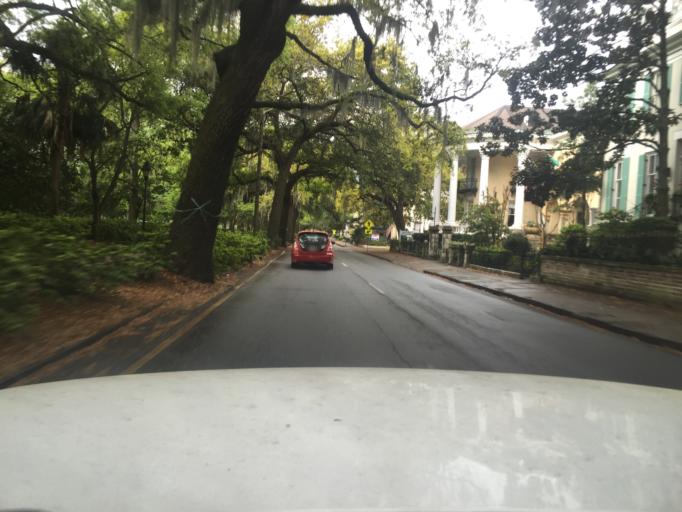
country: US
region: Georgia
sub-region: Chatham County
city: Savannah
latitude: 32.0701
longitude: -81.0965
